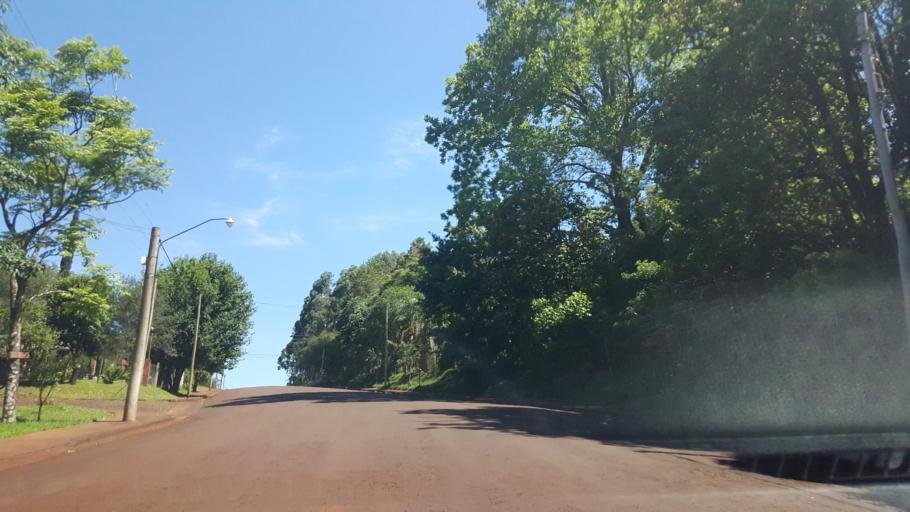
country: AR
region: Misiones
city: Capiovi
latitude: -26.9306
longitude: -55.0651
